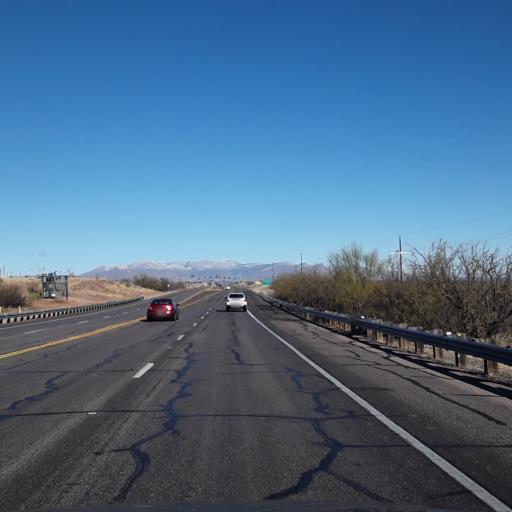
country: US
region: Arizona
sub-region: Cochise County
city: Sierra Vista
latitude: 31.5699
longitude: -110.3132
